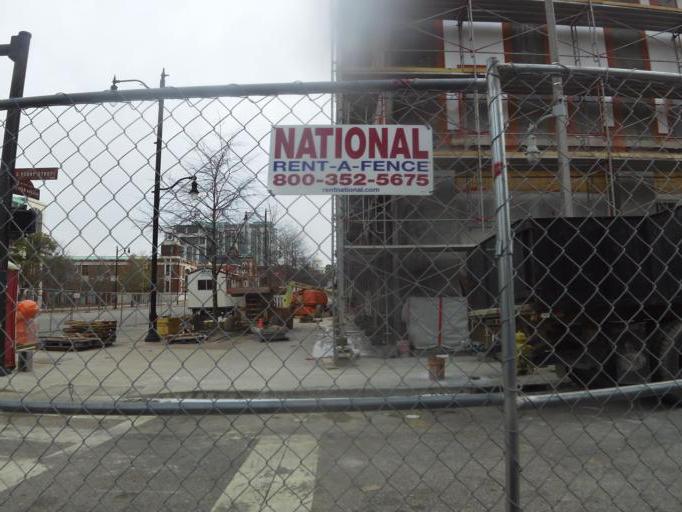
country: US
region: Alabama
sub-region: Montgomery County
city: Montgomery
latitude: 32.3773
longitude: -86.3074
